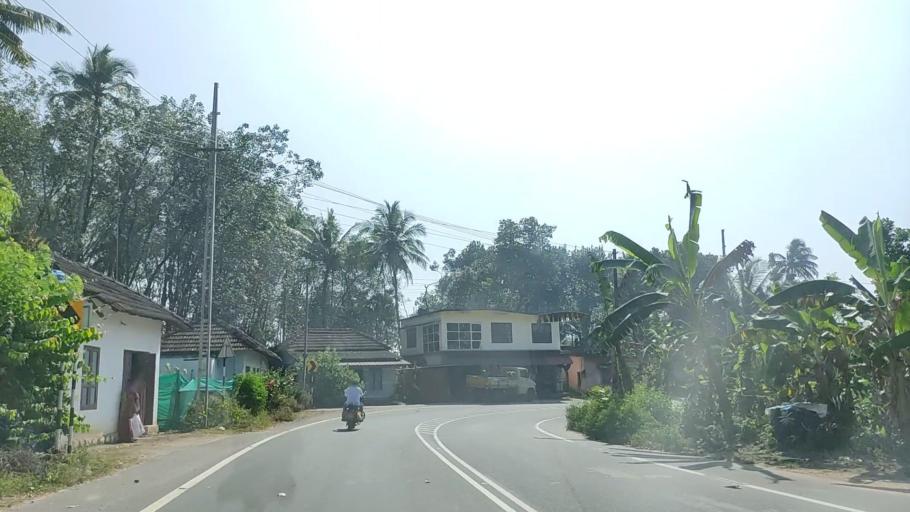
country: IN
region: Kerala
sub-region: Kollam
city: Punalur
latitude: 8.9321
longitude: 76.9992
